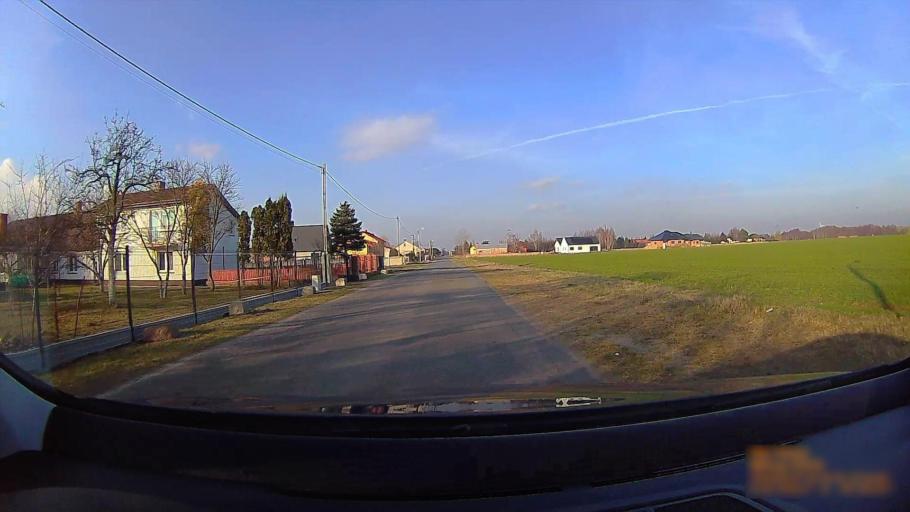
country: PL
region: Greater Poland Voivodeship
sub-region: Konin
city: Konin
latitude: 52.1793
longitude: 18.3008
